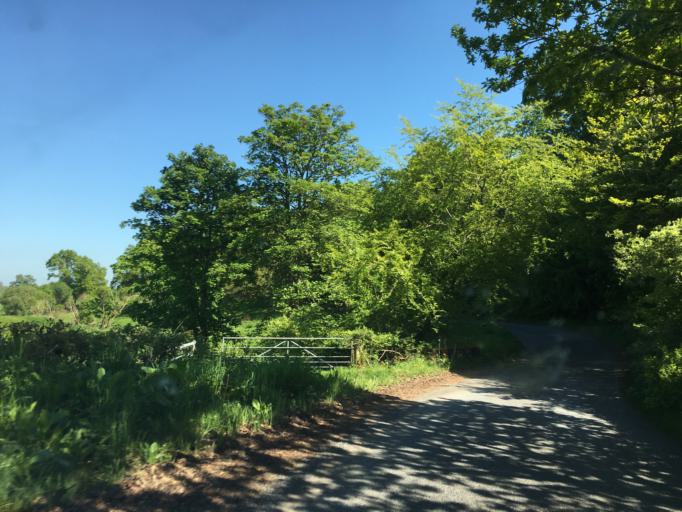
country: GB
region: Scotland
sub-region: Perth and Kinross
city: Methven
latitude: 56.4215
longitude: -3.6139
